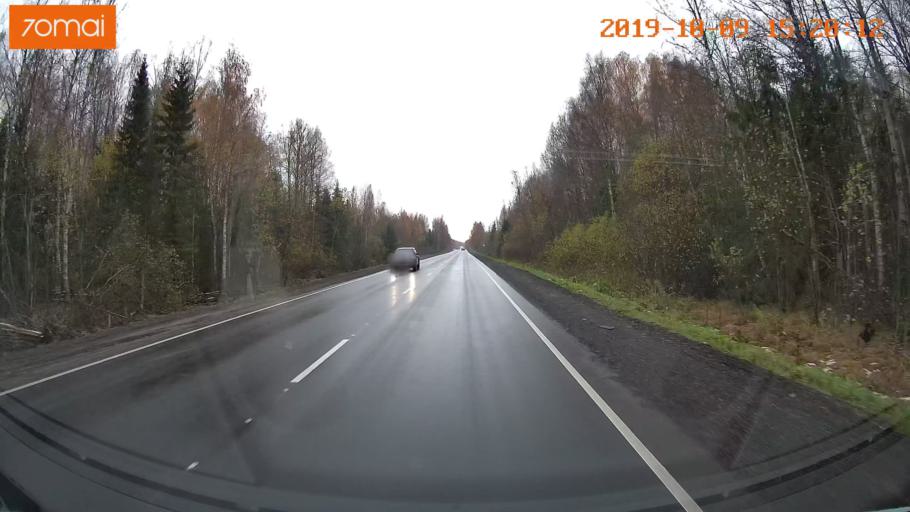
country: RU
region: Kostroma
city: Susanino
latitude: 58.0671
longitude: 41.5423
